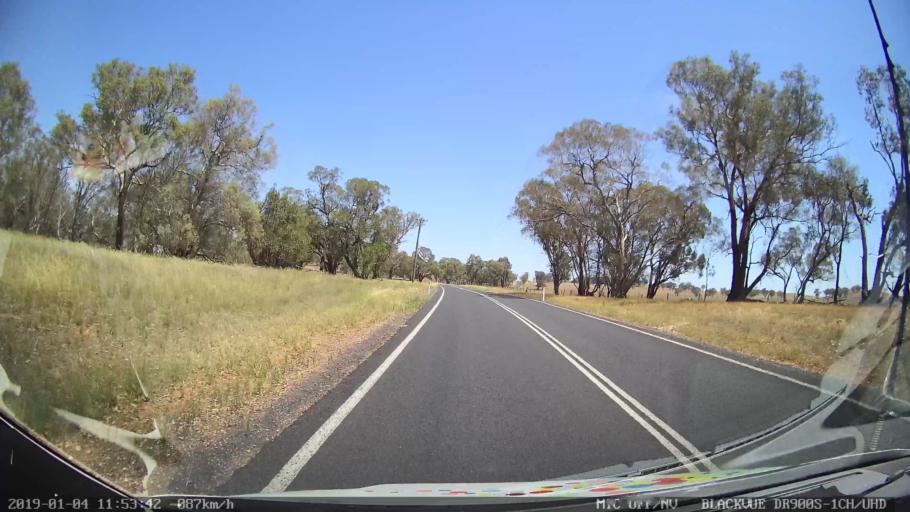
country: AU
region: New South Wales
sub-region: Cabonne
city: Molong
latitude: -32.8726
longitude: 148.7378
